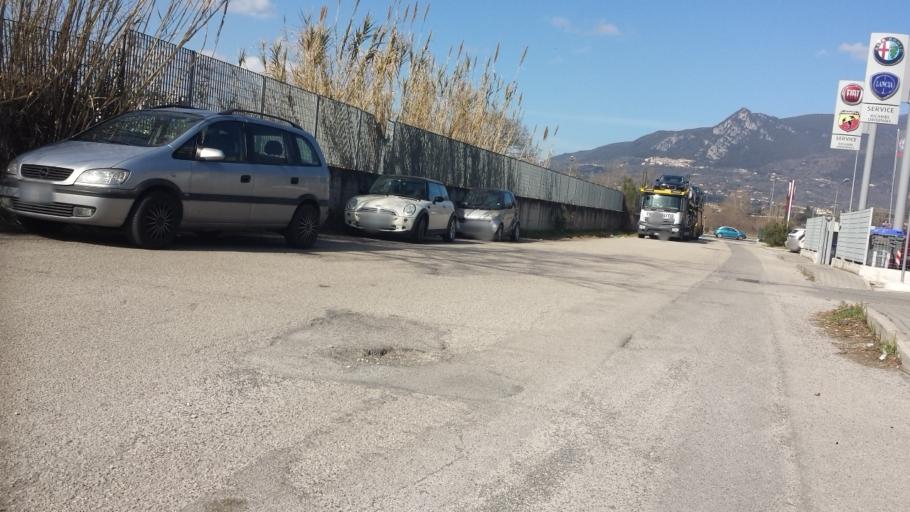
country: IT
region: Umbria
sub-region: Provincia di Terni
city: Terni
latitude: 42.5663
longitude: 12.5997
